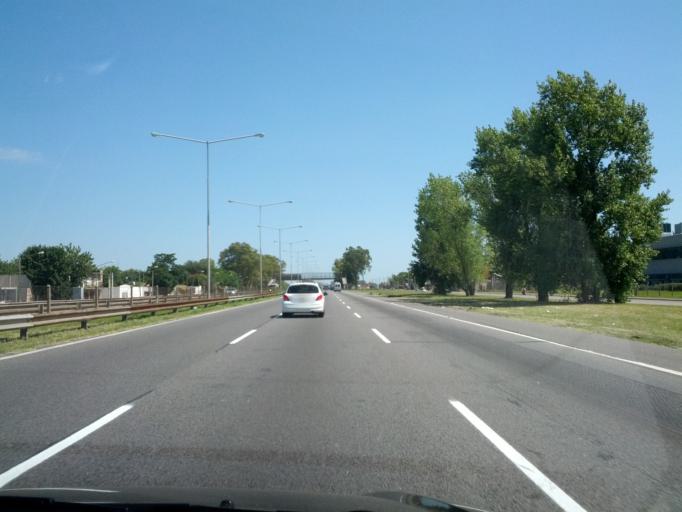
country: AR
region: Buenos Aires
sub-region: Partido de Campana
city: Campana
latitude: -34.2075
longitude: -58.9318
